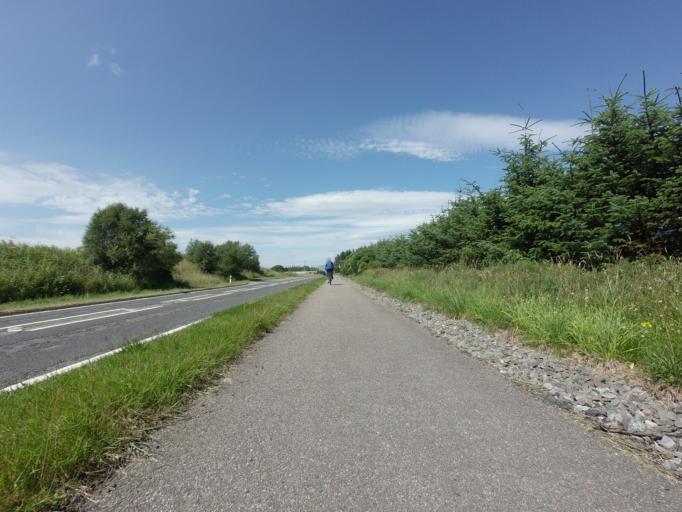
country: GB
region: Scotland
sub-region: Highland
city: Conon Bridge
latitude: 57.5448
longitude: -4.3828
